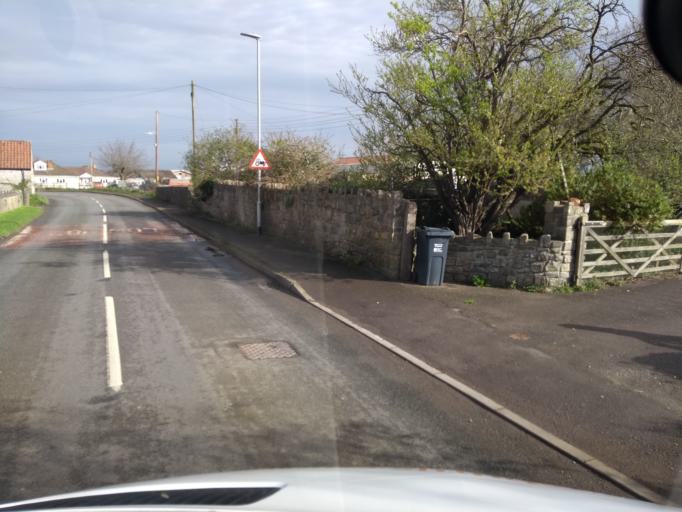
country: GB
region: England
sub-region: Somerset
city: Woolavington
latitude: 51.1713
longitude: -2.9344
